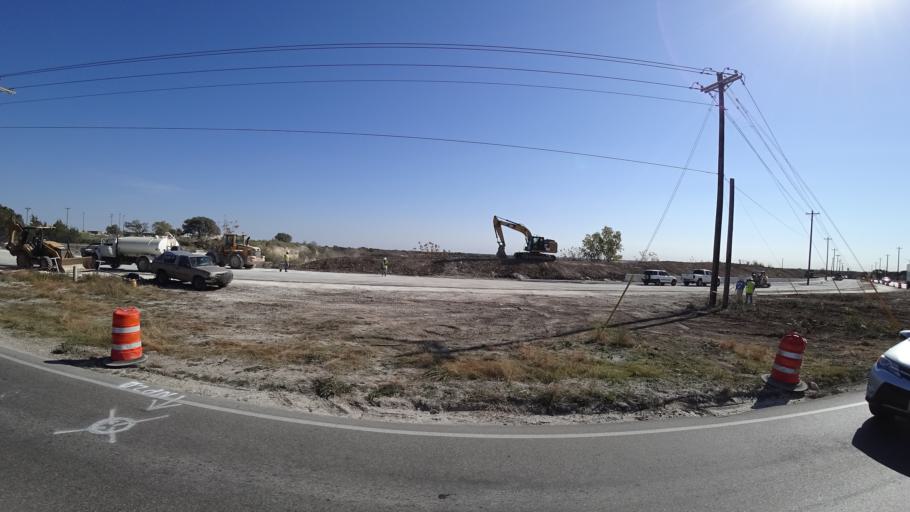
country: US
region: Texas
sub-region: Williamson County
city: Cedar Park
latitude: 30.5014
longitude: -97.8586
